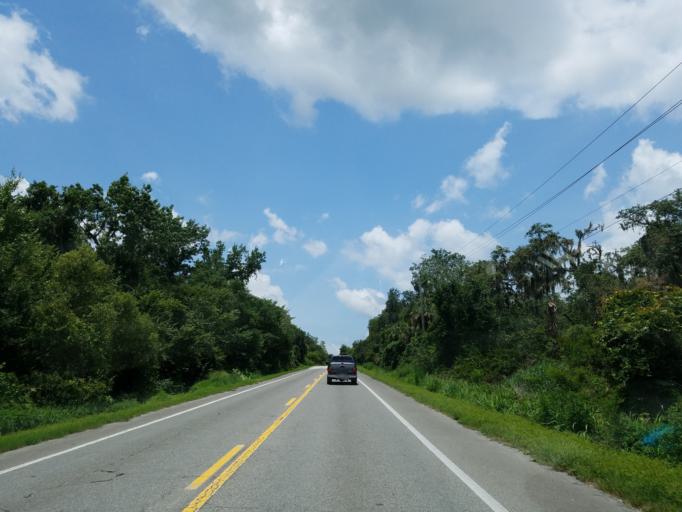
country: US
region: Florida
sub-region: Hillsborough County
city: Fish Hawk
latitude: 27.8506
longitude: -82.1184
